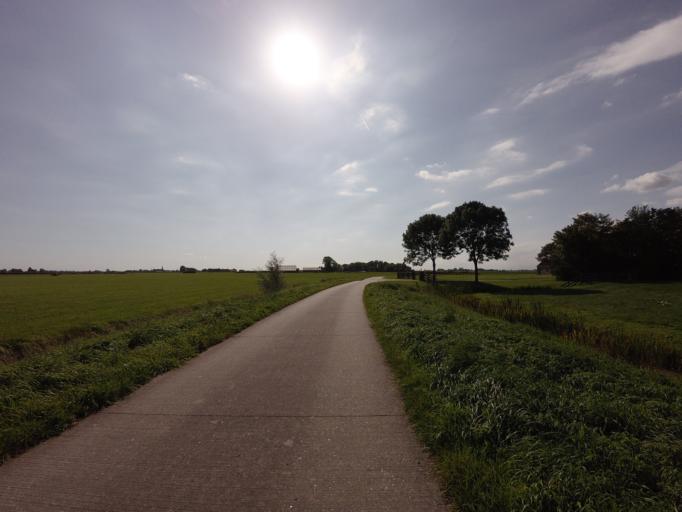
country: NL
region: Friesland
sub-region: Gemeente Littenseradiel
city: Makkum
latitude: 53.0928
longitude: 5.6388
